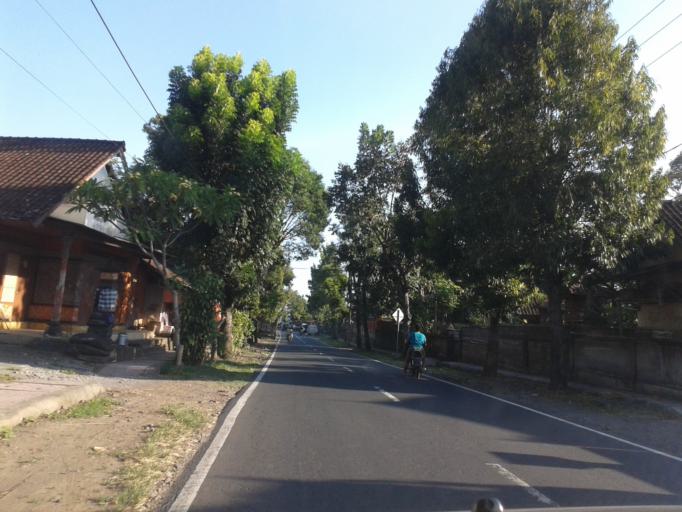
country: ID
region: Bali
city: Banjar Wangsian
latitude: -8.4987
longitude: 115.4033
